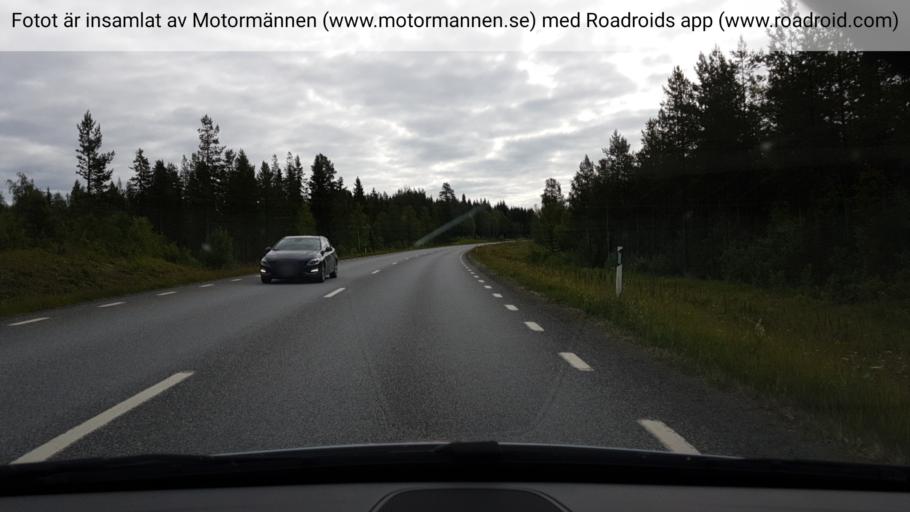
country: SE
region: Jaemtland
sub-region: OEstersunds Kommun
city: Lit
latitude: 63.3981
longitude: 14.9877
